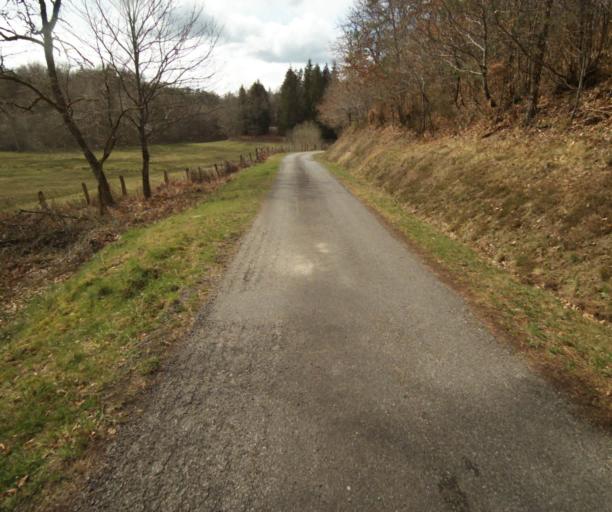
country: FR
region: Limousin
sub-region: Departement de la Correze
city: Argentat
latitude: 45.2196
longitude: 1.9154
